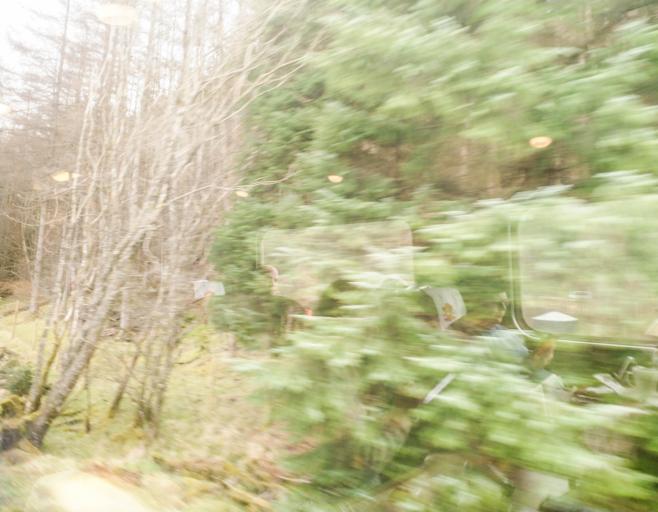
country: GB
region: Scotland
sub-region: Argyll and Bute
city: Garelochhead
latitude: 56.4448
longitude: -4.7079
